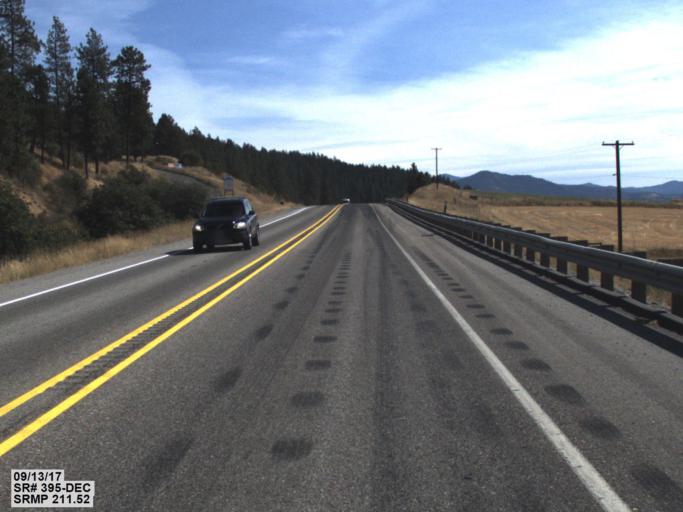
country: US
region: Washington
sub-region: Stevens County
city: Chewelah
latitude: 48.3102
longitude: -117.7888
